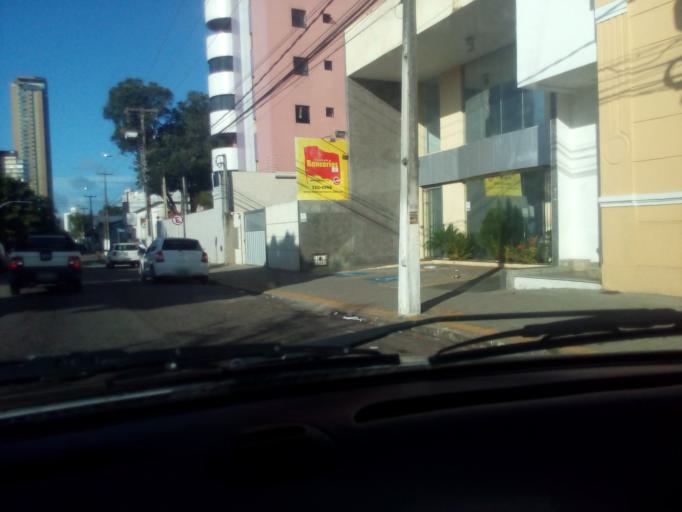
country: BR
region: Rio Grande do Norte
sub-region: Natal
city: Natal
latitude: -5.7837
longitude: -35.2027
